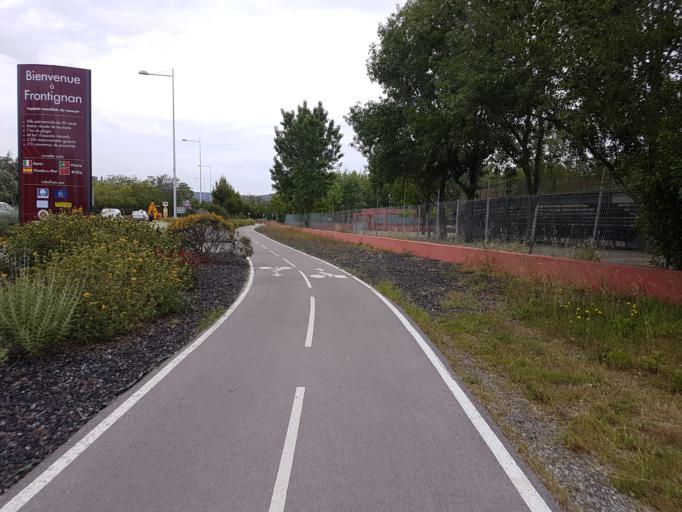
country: FR
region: Languedoc-Roussillon
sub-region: Departement de l'Herault
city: Frontignan
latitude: 43.4403
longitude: 3.7595
